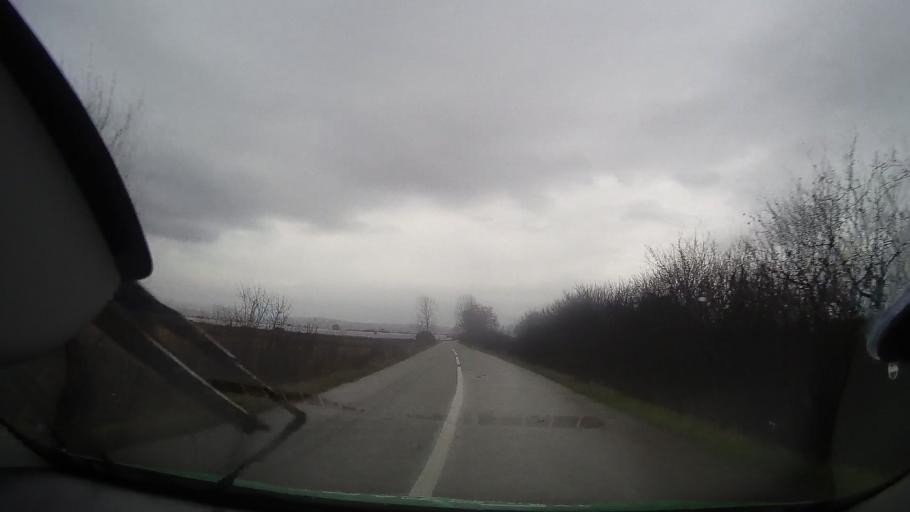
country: RO
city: Capalna
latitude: 46.7254
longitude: 22.0886
